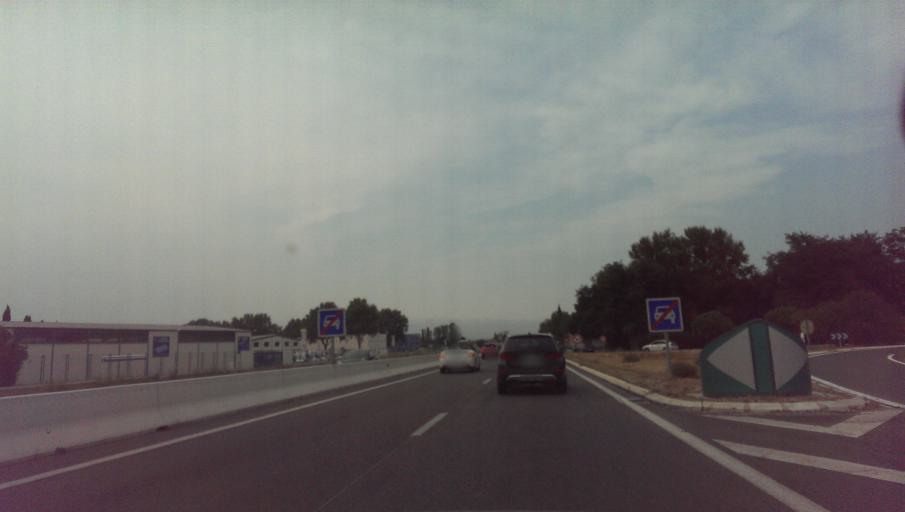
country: FR
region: Languedoc-Roussillon
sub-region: Departement des Pyrenees-Orientales
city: Rivesaltes
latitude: 42.7681
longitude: 2.9000
